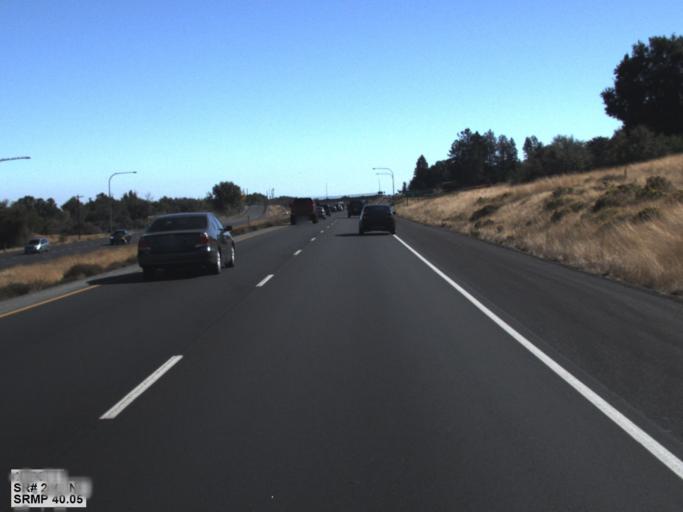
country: US
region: Washington
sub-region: Franklin County
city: West Pasco
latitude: 46.2300
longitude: -119.1999
